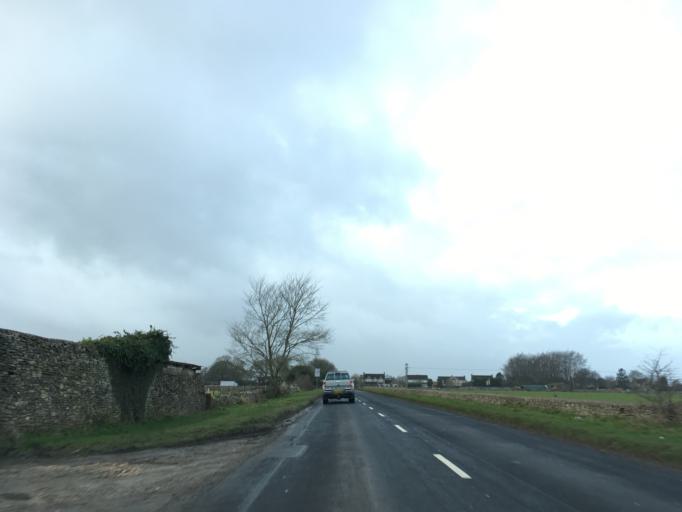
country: GB
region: England
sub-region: Gloucestershire
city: Minchinhampton
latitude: 51.7093
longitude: -2.1701
